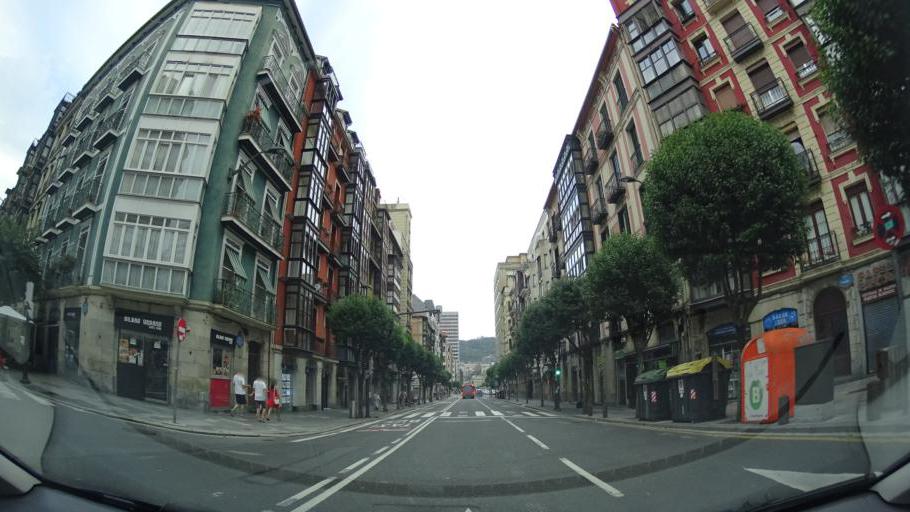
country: ES
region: Basque Country
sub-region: Bizkaia
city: Bilbao
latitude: 43.2584
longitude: -2.9323
